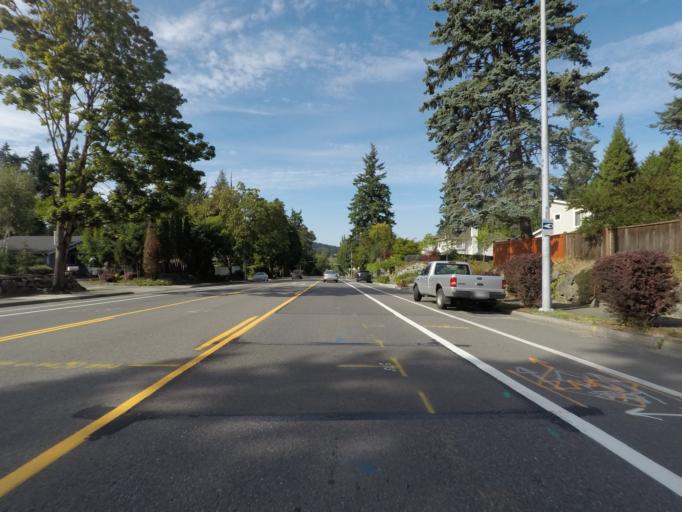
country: US
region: Washington
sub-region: King County
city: Kirkland
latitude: 47.6938
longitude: -122.2100
